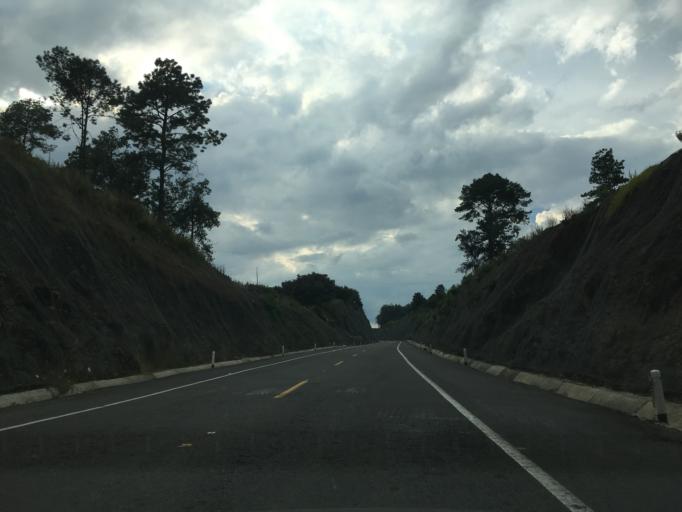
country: MX
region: Michoacan
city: Angahuan
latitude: 19.5077
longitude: -102.1532
